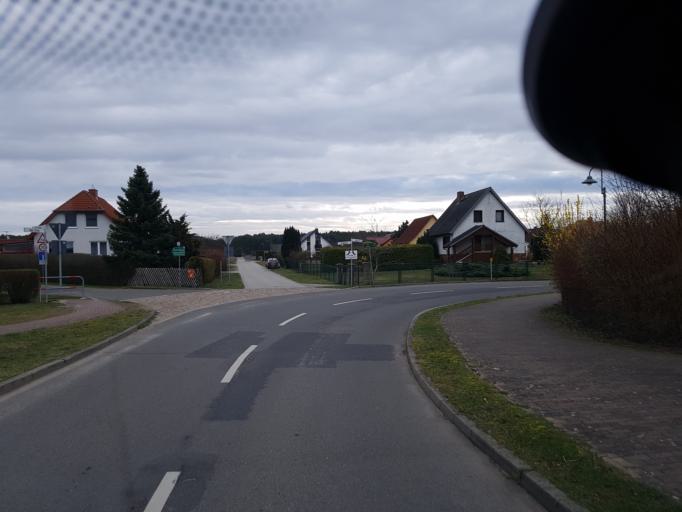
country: DE
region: Brandenburg
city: Mixdorf
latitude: 52.1958
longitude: 14.4112
